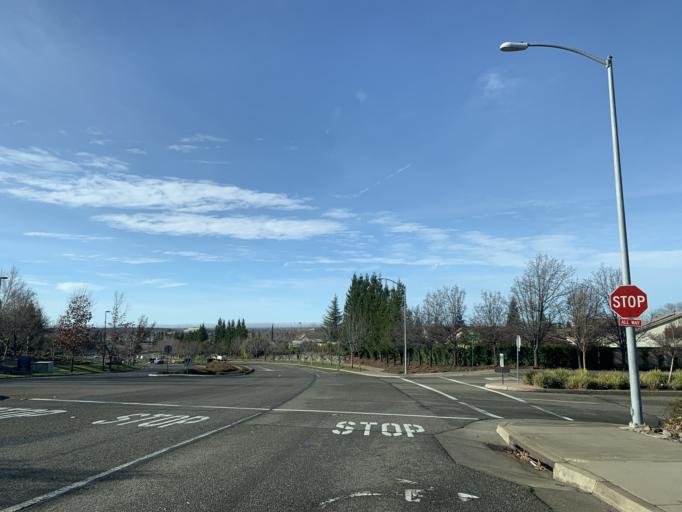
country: US
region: California
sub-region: El Dorado County
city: El Dorado Hills
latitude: 38.6582
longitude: -121.1156
